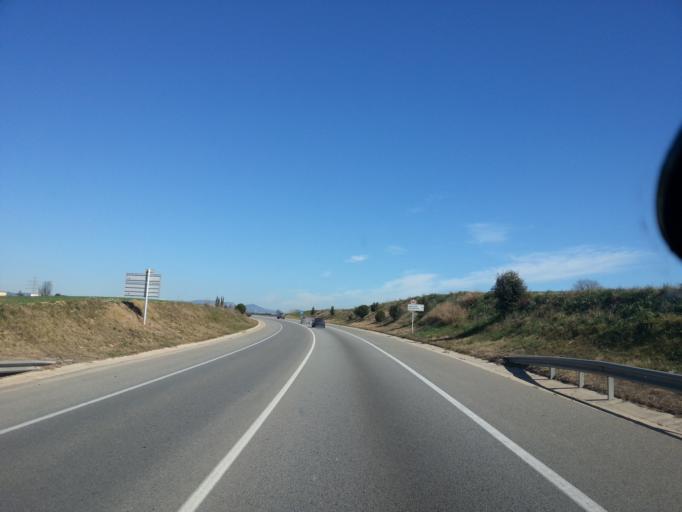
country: ES
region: Catalonia
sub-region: Provincia de Barcelona
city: Santa Perpetua de Mogoda
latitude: 41.5607
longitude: 2.1873
